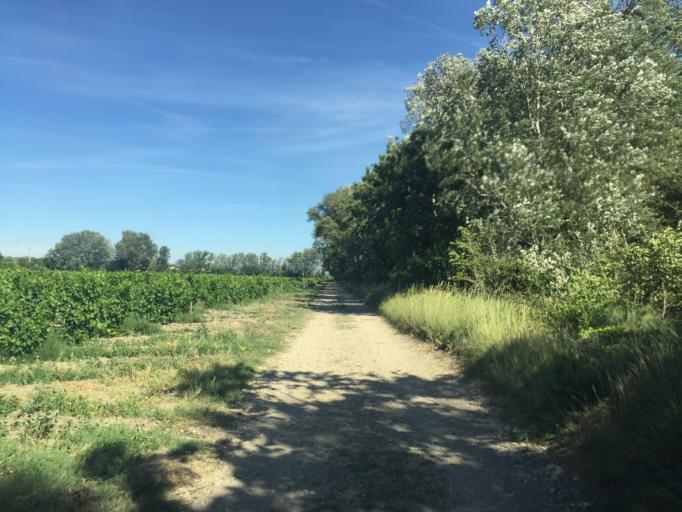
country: FR
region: Provence-Alpes-Cote d'Azur
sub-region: Departement du Vaucluse
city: Chateauneuf-du-Pape
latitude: 44.0438
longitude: 4.8209
